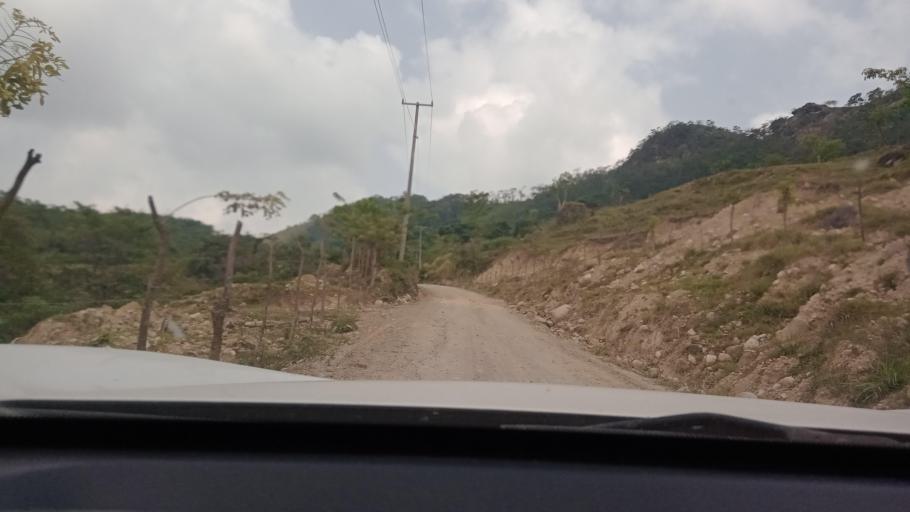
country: MX
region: Tabasco
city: Chontalpa
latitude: 17.4943
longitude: -93.6568
